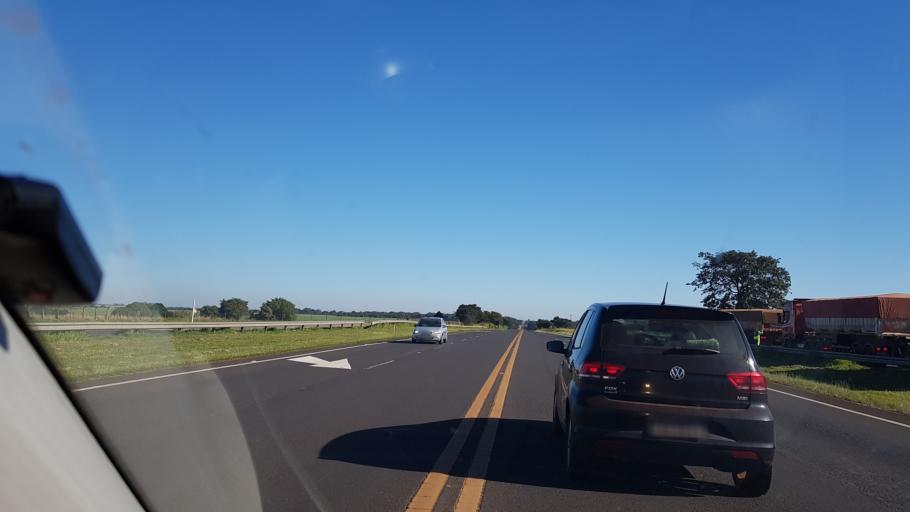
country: BR
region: Sao Paulo
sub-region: Assis
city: Assis
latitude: -22.5957
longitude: -50.4867
